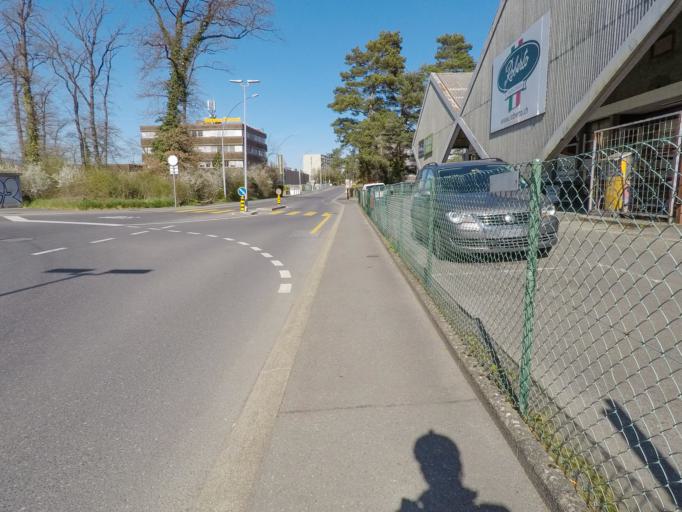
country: CH
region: Geneva
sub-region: Geneva
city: Meyrin
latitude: 46.2250
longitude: 6.0769
